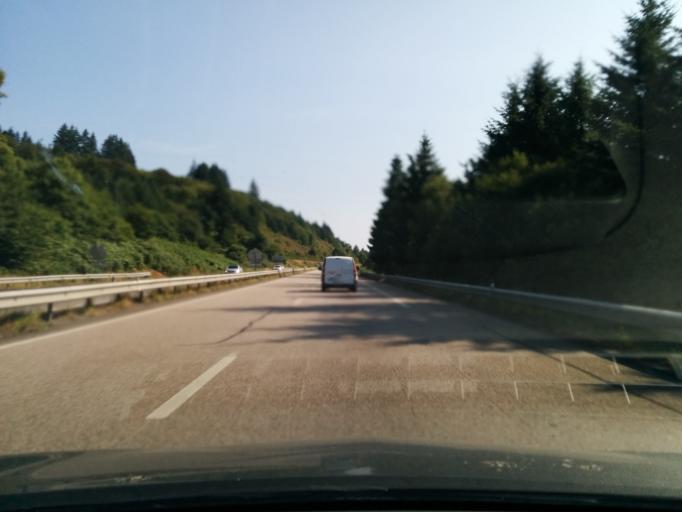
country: FR
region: Limousin
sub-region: Departement de la Haute-Vienne
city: Bonnac-la-Cote
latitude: 45.9718
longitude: 1.3210
